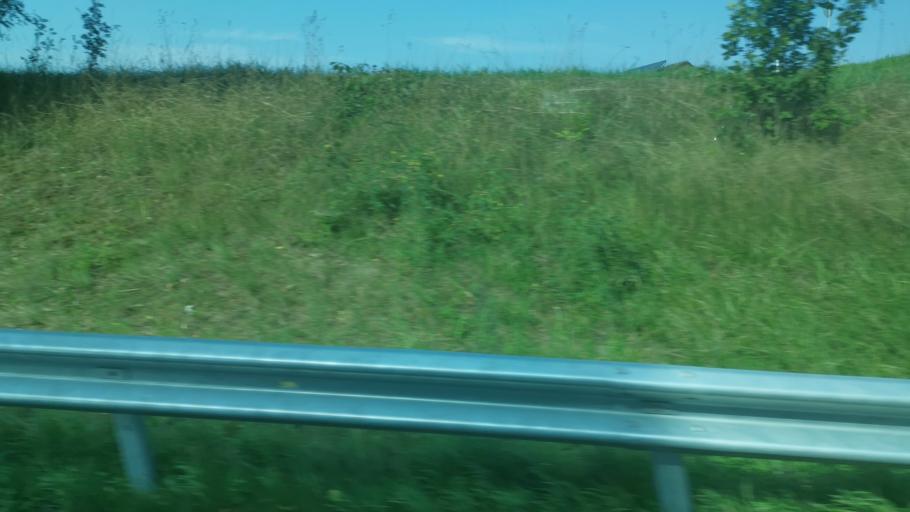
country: DE
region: Bavaria
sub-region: Upper Palatinate
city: Willmering
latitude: 49.2373
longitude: 12.6750
